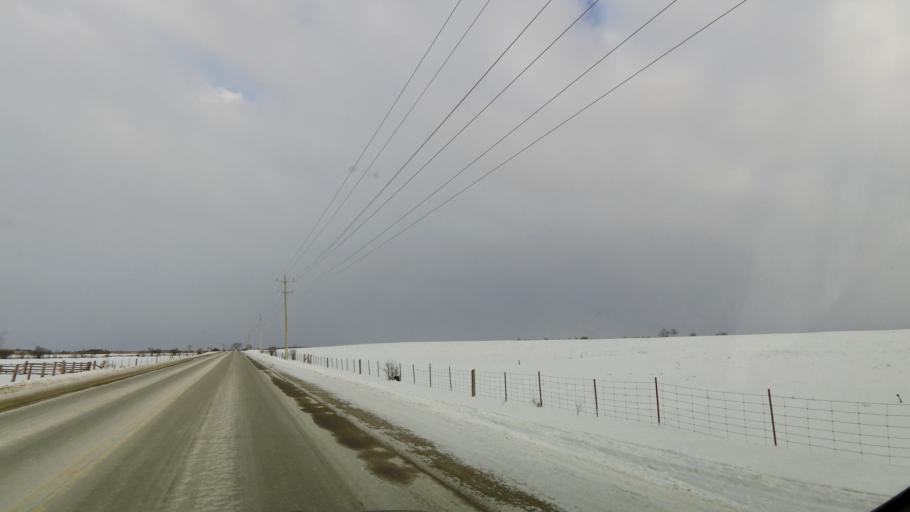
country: CA
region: Ontario
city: Omemee
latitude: 44.4759
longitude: -78.9078
